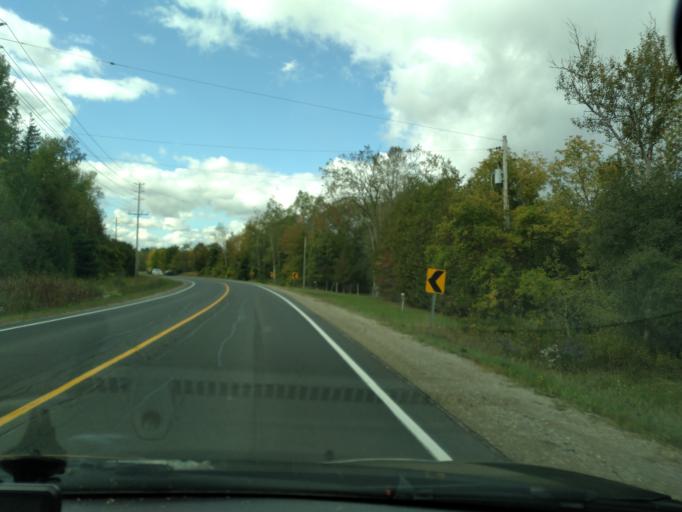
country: CA
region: Ontario
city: Angus
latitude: 44.2568
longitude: -79.7883
